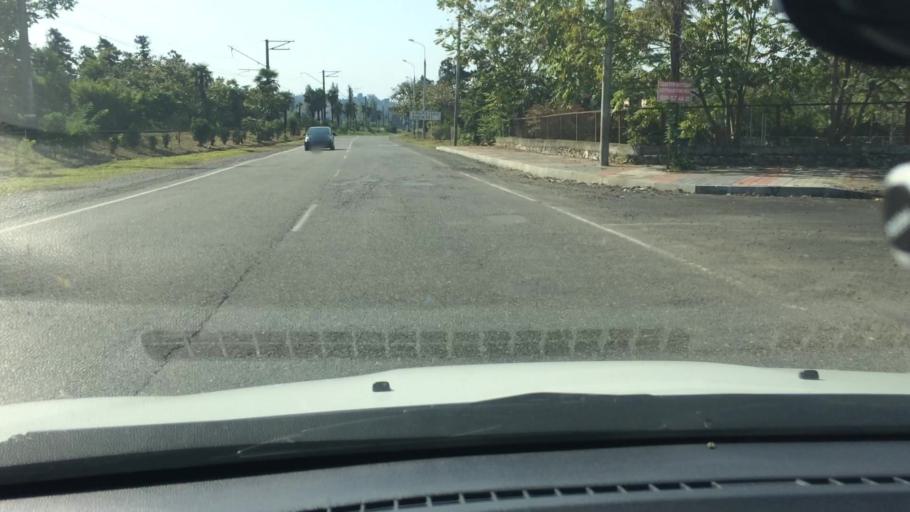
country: GE
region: Ajaria
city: Kobuleti
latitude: 41.7953
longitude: 41.7711
